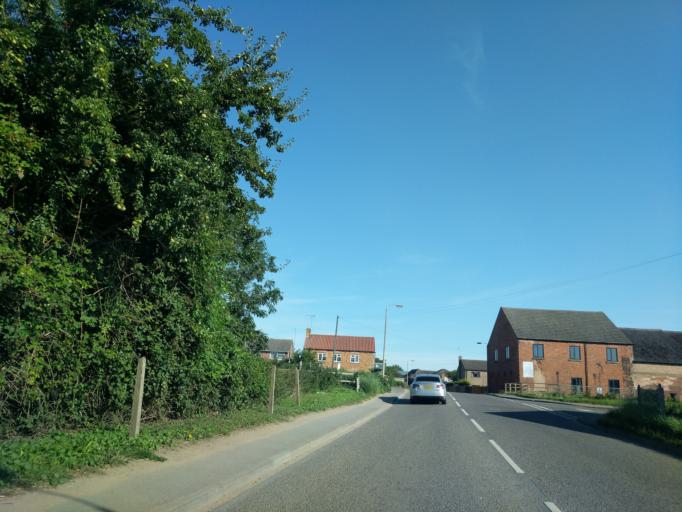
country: GB
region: England
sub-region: Lincolnshire
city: Bourne
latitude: 52.7650
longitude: -0.3624
